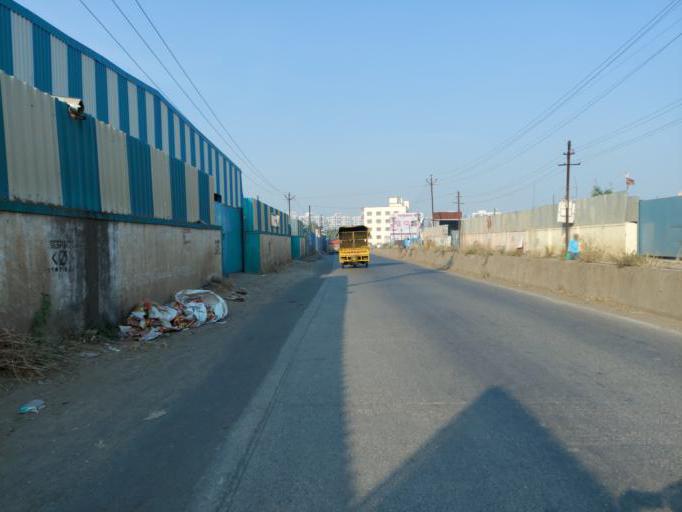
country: IN
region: Maharashtra
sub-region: Pune Division
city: Pune
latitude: 18.4573
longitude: 73.9413
